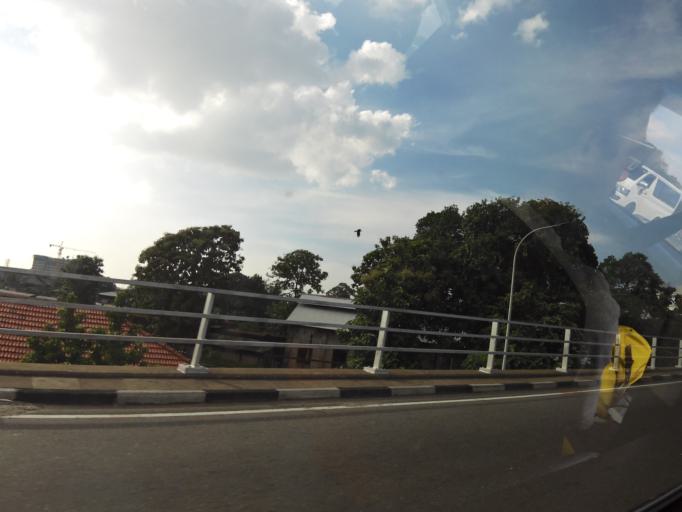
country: LK
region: Western
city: Kolonnawa
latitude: 6.9359
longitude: 79.8781
